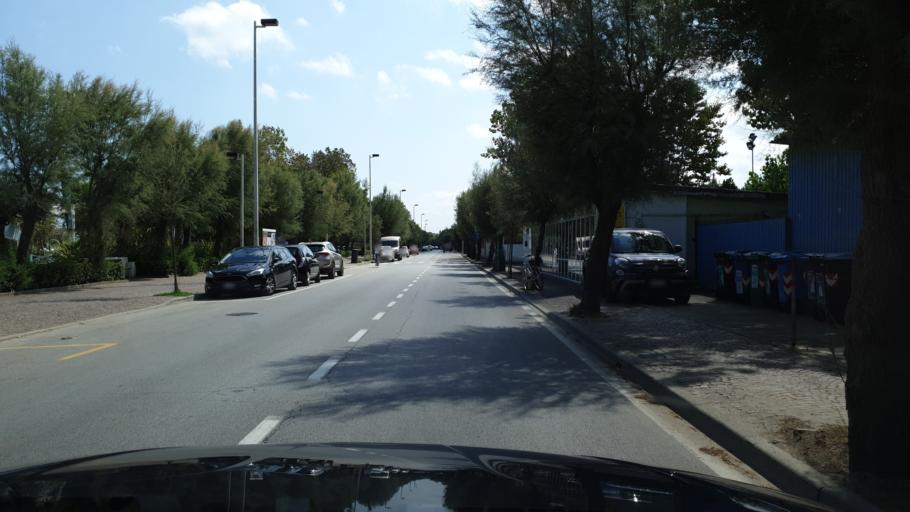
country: IT
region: Emilia-Romagna
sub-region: Provincia di Rimini
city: Riccione
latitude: 43.9928
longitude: 12.6761
